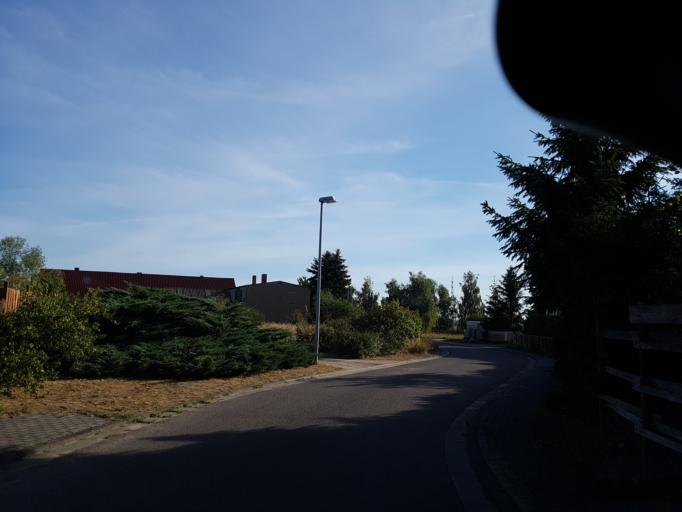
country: DE
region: Saxony
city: Nauwalde
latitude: 51.4476
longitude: 13.4188
